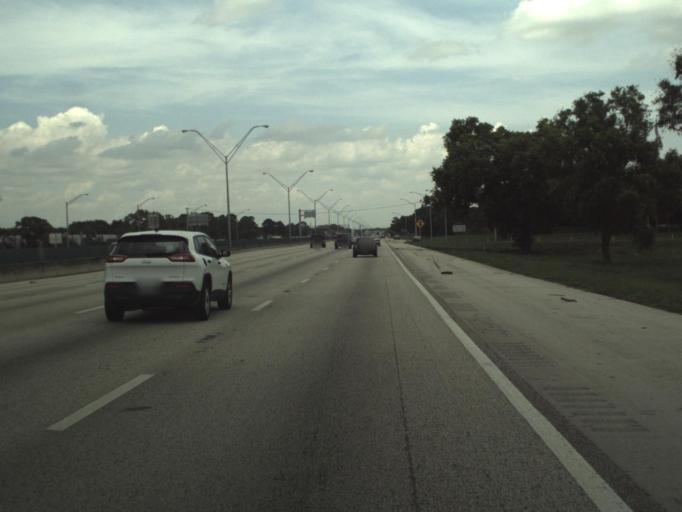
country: US
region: Florida
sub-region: Broward County
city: Deerfield Beach
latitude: 26.3219
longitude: -80.1163
